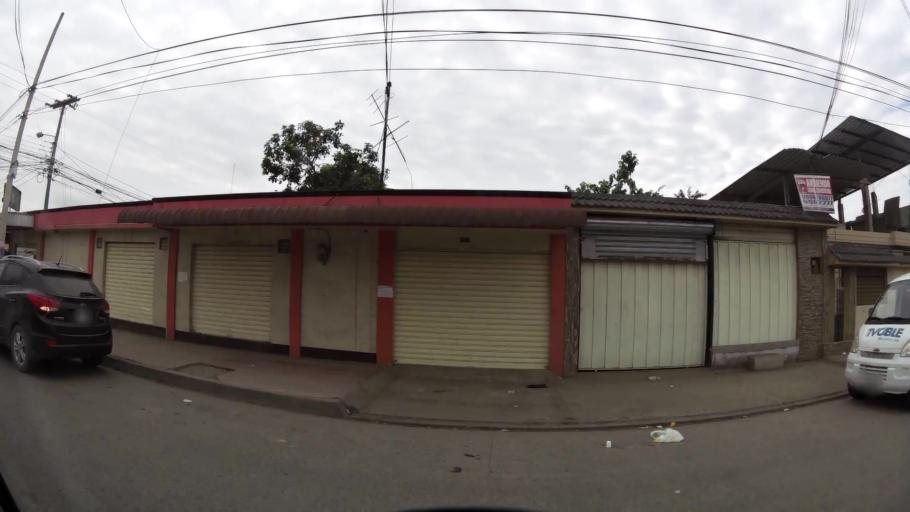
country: EC
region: El Oro
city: Machala
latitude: -3.2507
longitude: -79.9582
